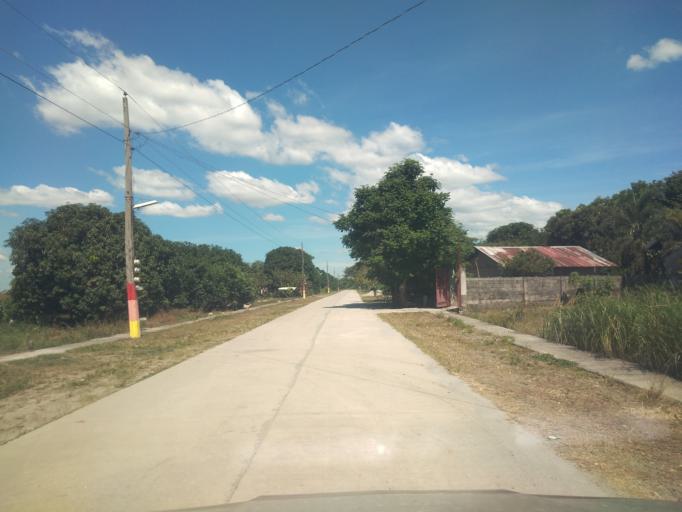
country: PH
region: Central Luzon
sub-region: Province of Pampanga
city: San Basilio
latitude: 15.0300
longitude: 120.6057
